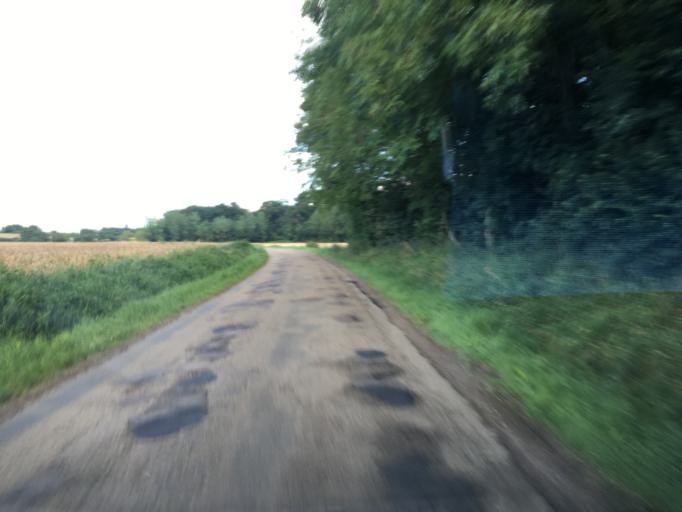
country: FR
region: Bourgogne
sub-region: Departement de l'Yonne
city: Appoigny
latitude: 47.8807
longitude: 3.5055
